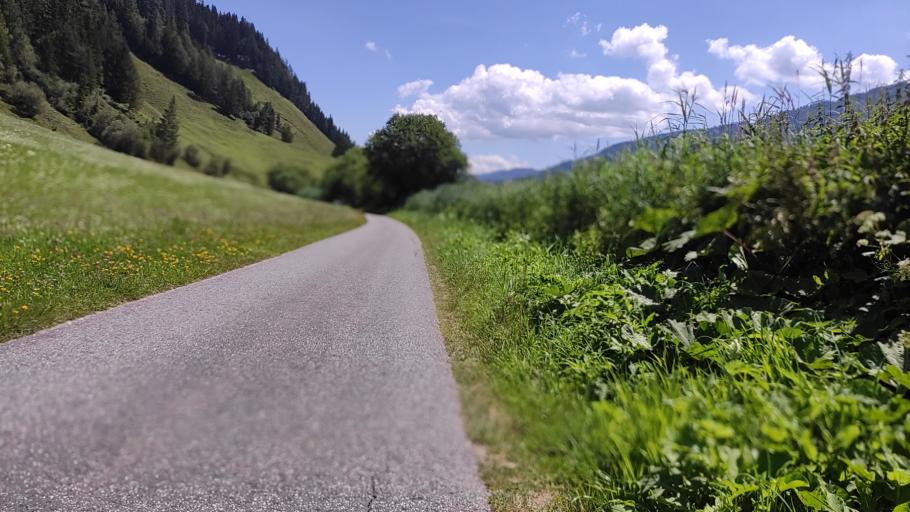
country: AT
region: Tyrol
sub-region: Politischer Bezirk Kitzbuhel
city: Hochfilzen
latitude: 47.4640
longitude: 12.6390
